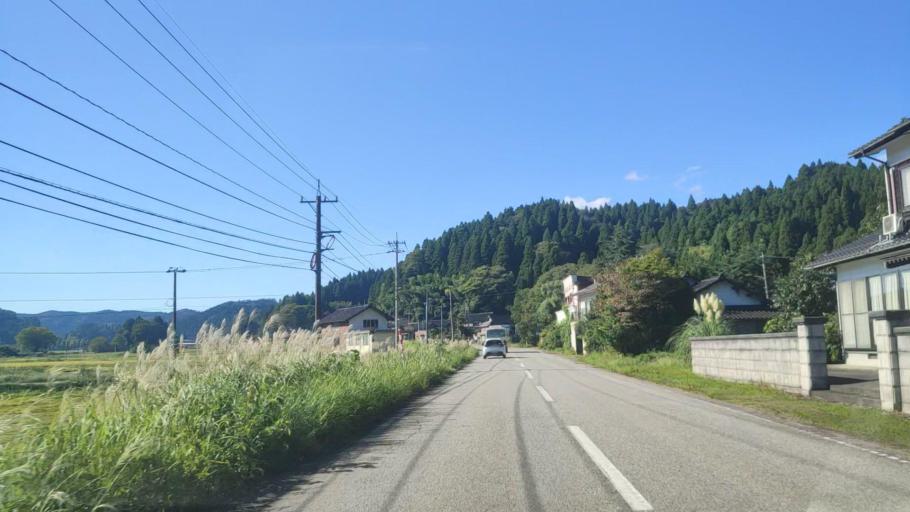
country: JP
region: Ishikawa
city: Nanao
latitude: 37.2767
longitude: 137.0530
